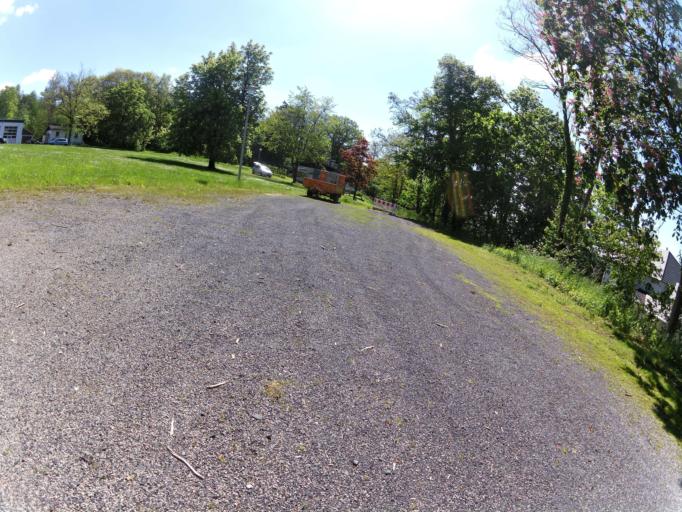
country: DE
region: Thuringia
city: Dankmarshausen
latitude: 50.9536
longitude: 10.0330
